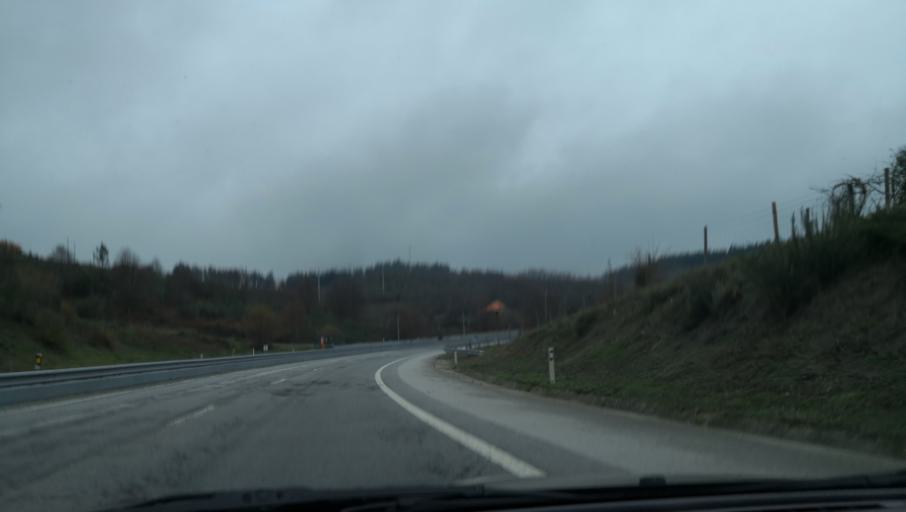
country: PT
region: Viseu
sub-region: Lamego
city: Lamego
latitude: 41.0751
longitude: -7.8105
